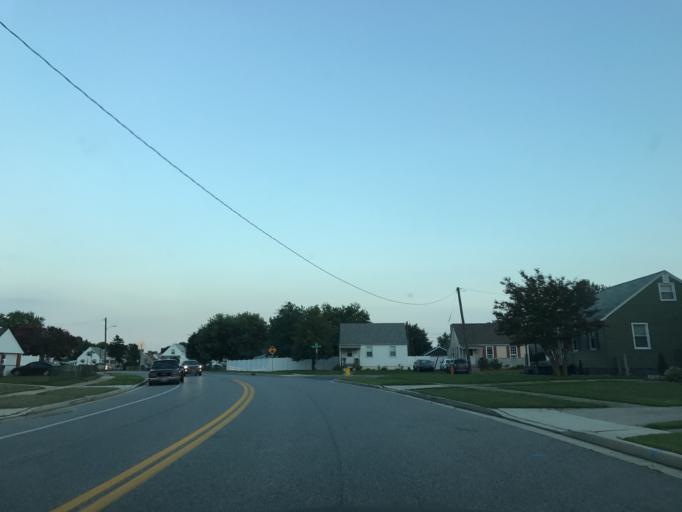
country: US
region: Maryland
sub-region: Baltimore County
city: Dundalk
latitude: 39.2794
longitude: -76.5262
